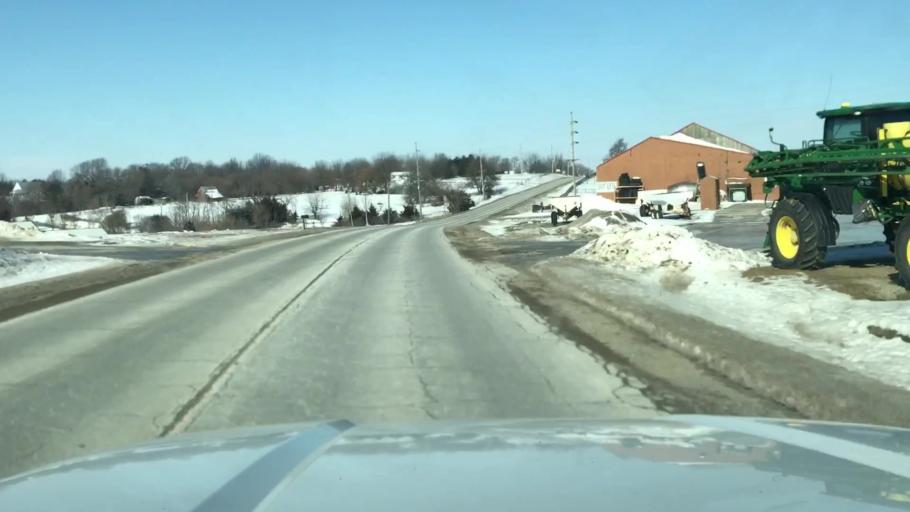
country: US
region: Missouri
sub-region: Andrew County
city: Savannah
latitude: 39.9508
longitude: -94.8457
